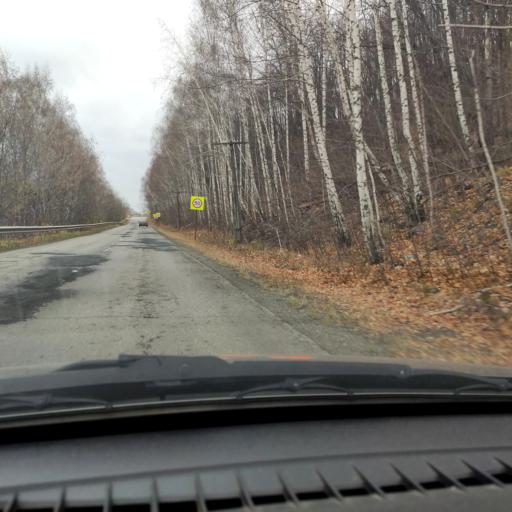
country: RU
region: Samara
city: Pribrezhnyy
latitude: 53.4416
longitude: 49.7642
